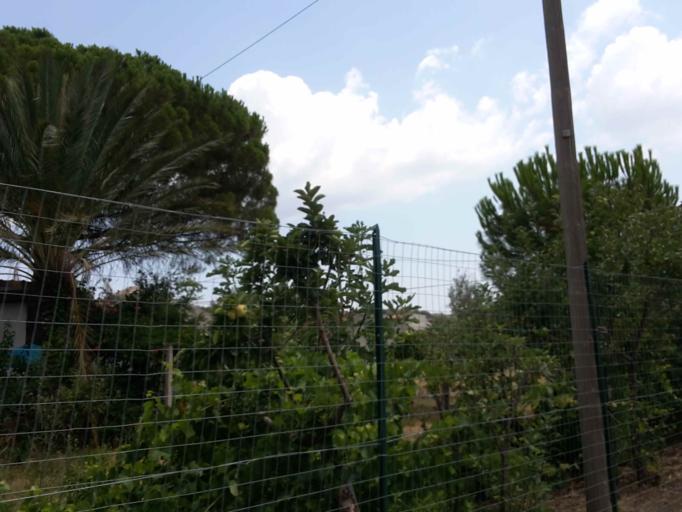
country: IT
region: Calabria
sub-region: Provincia di Reggio Calabria
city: Condofuri
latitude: 37.9870
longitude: 15.8409
